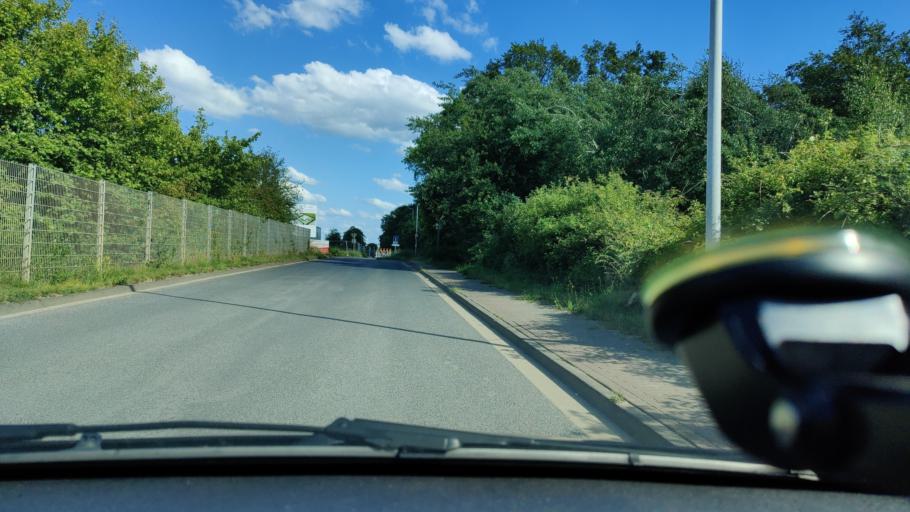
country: DE
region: North Rhine-Westphalia
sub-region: Regierungsbezirk Dusseldorf
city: Kamp-Lintfort
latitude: 51.5229
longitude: 6.5681
